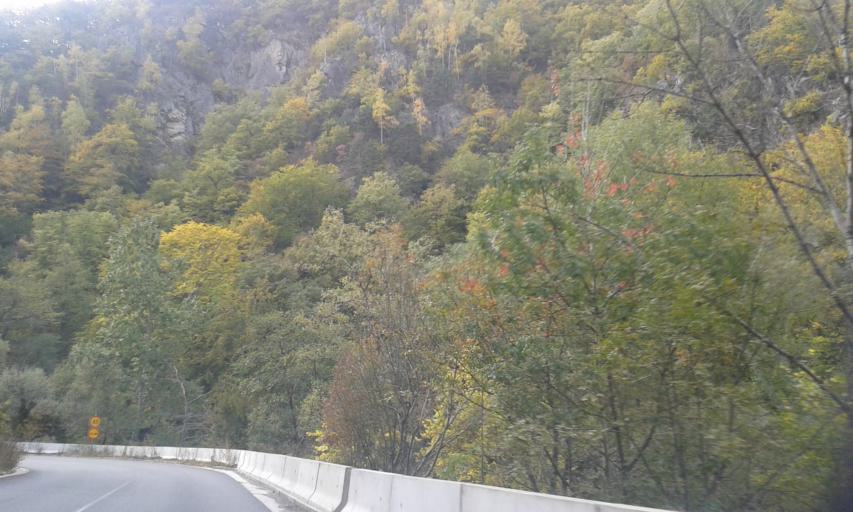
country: RO
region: Gorj
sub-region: Comuna Bumbesti-Jiu
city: Bumbesti-Jiu
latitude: 45.2059
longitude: 23.3743
